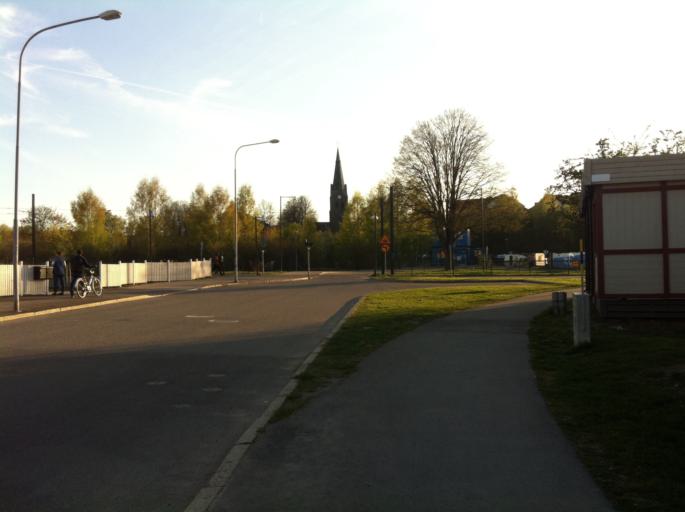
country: SE
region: OEstergoetland
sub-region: Norrkopings Kommun
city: Norrkoping
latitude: 58.5780
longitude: 16.2018
